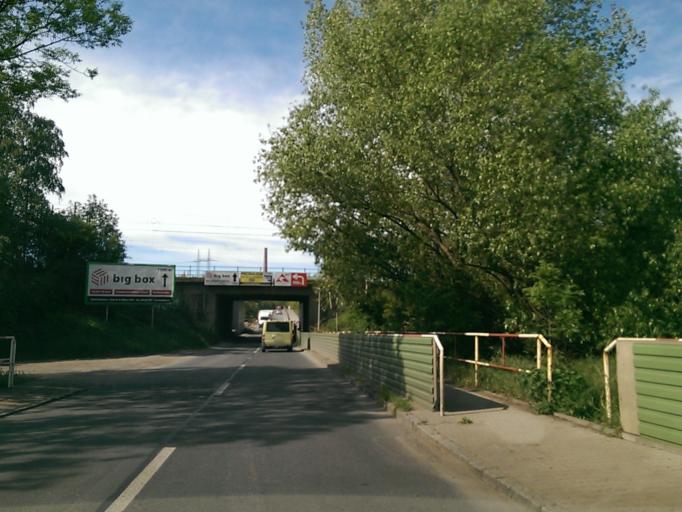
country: CZ
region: Praha
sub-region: Praha 20
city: Horni Pocernice
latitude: 50.0828
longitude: 14.6165
